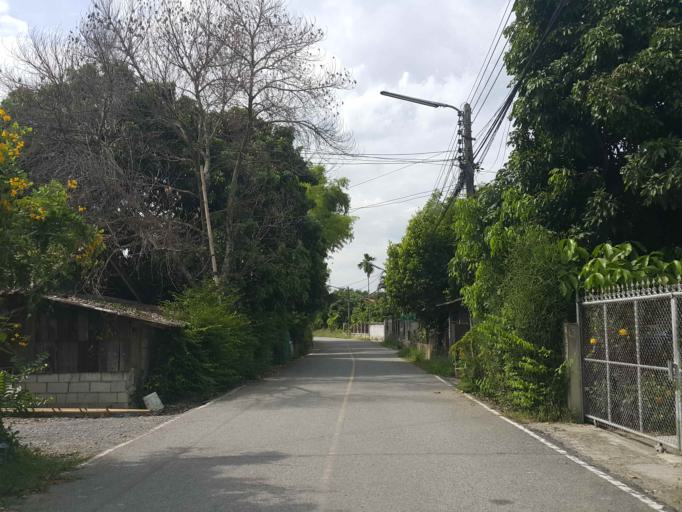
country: TH
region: Chiang Mai
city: Saraphi
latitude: 18.7384
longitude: 99.0565
